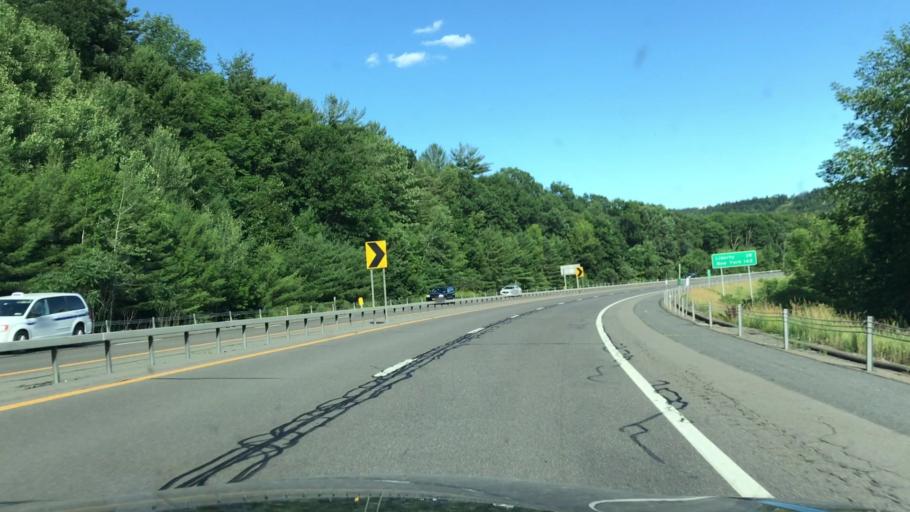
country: US
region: New York
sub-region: Delaware County
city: Hancock
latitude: 41.9599
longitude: -75.2806
